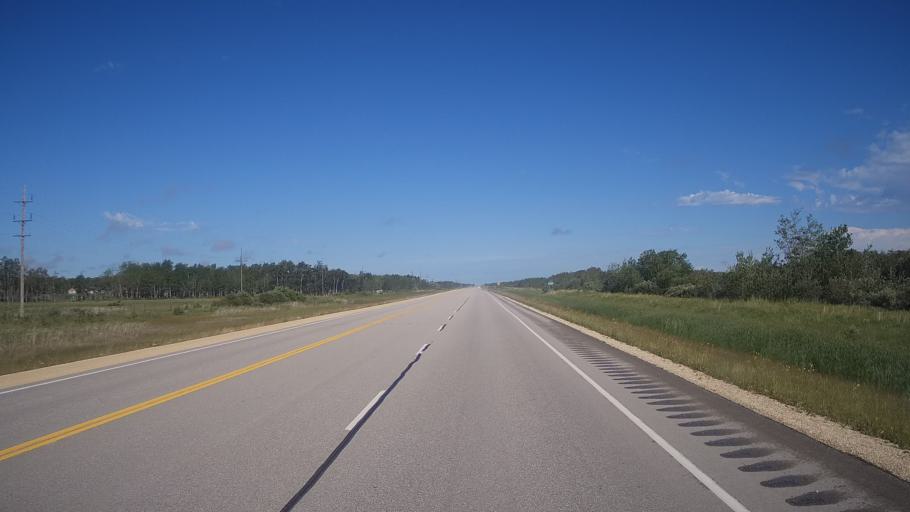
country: CA
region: Manitoba
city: Stonewall
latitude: 50.2306
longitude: -97.6984
